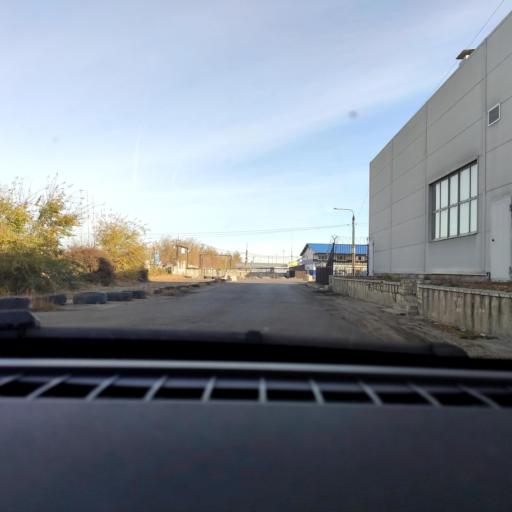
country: RU
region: Voronezj
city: Somovo
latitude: 51.6726
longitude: 39.2992
